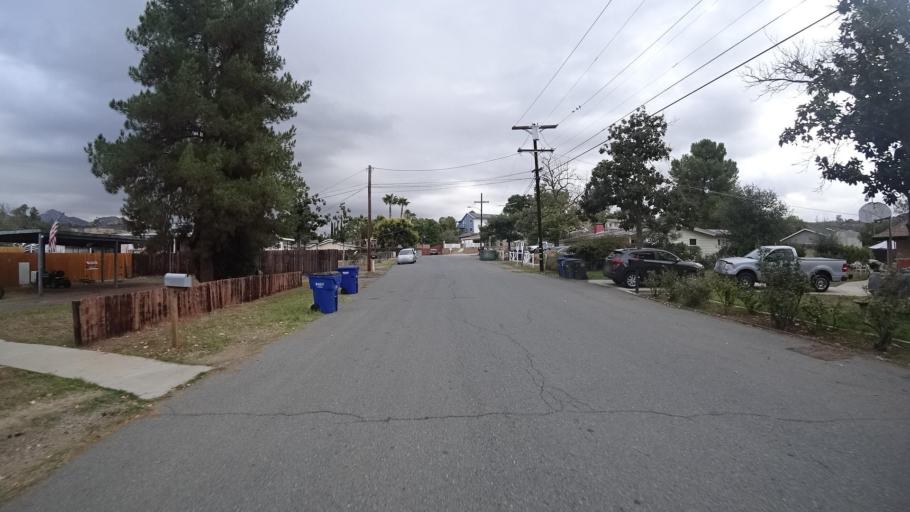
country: US
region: California
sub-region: San Diego County
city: Lakeside
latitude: 32.8581
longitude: -116.9070
